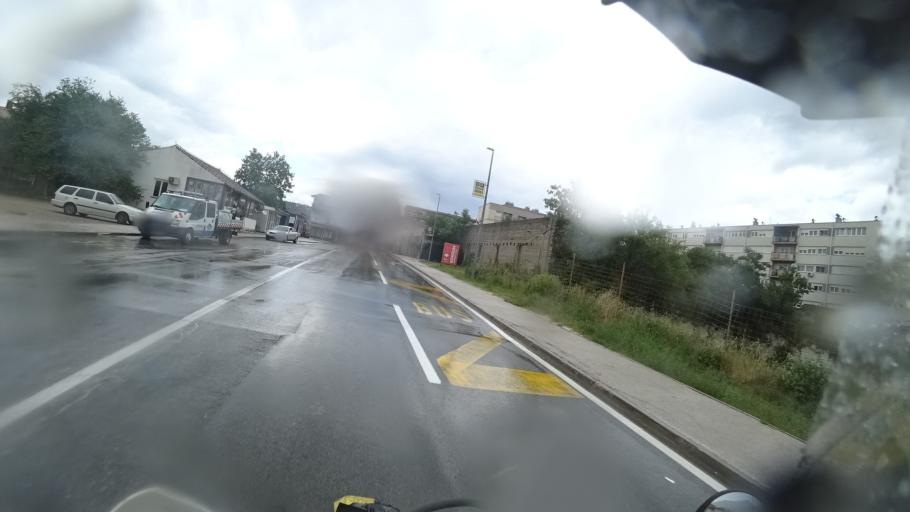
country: HR
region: Sibensko-Kniniska
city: Knin
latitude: 44.0421
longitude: 16.1984
